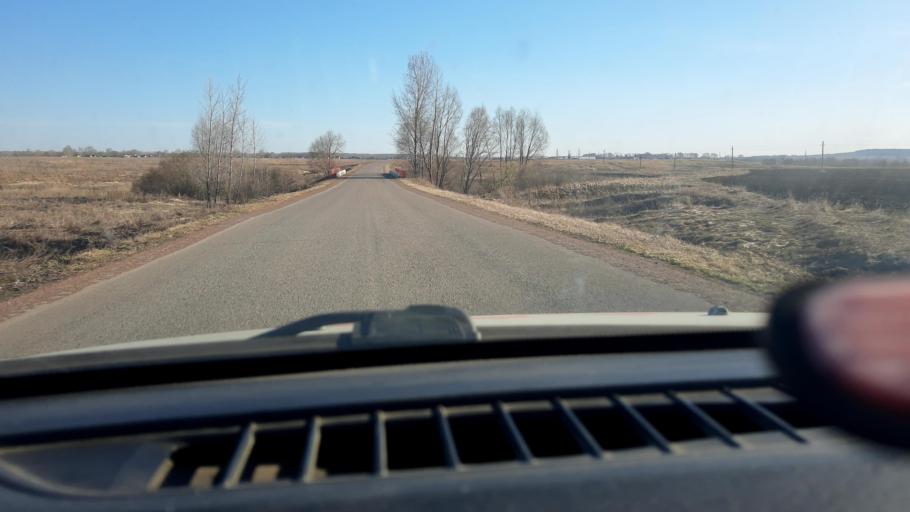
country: RU
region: Bashkortostan
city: Asanovo
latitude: 54.9432
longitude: 55.5193
